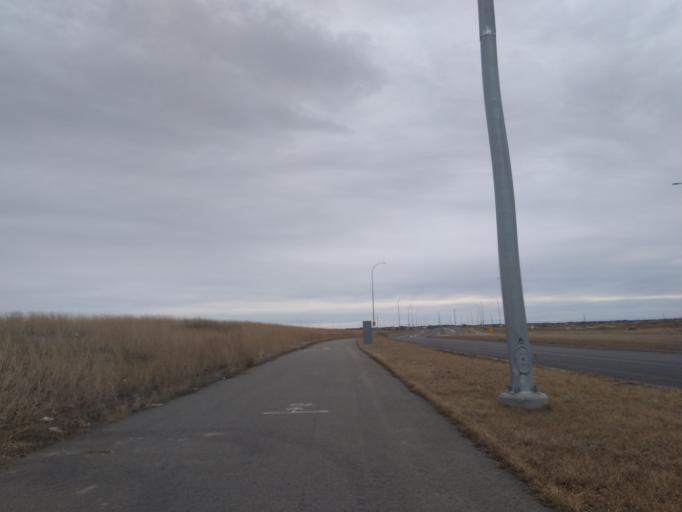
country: CA
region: Alberta
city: Airdrie
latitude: 51.1686
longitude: -113.9865
